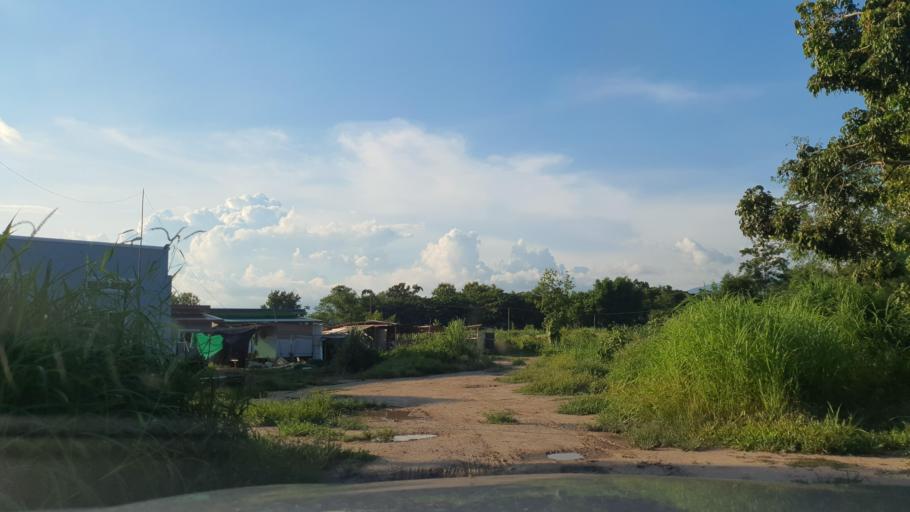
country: TH
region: Chiang Mai
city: Hang Dong
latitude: 18.6821
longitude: 98.8857
